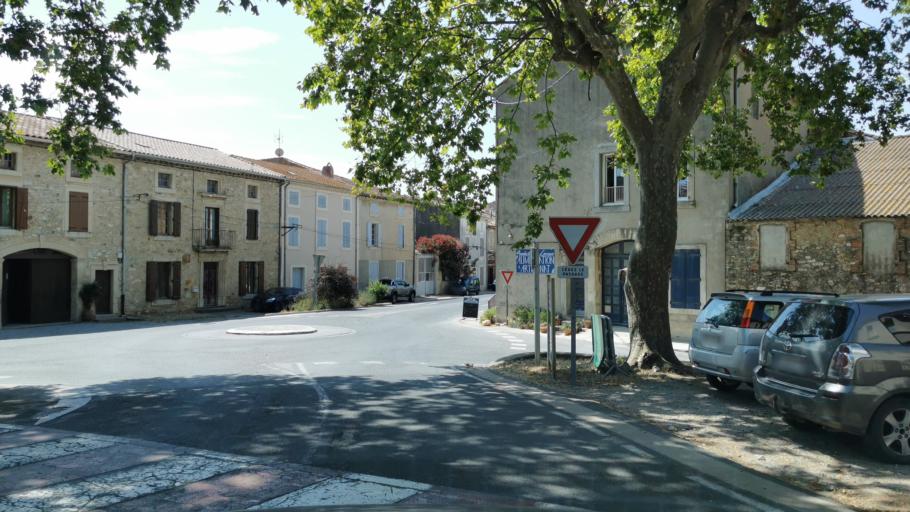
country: FR
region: Languedoc-Roussillon
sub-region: Departement de l'Aude
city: Bize-Minervois
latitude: 43.3162
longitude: 2.8705
